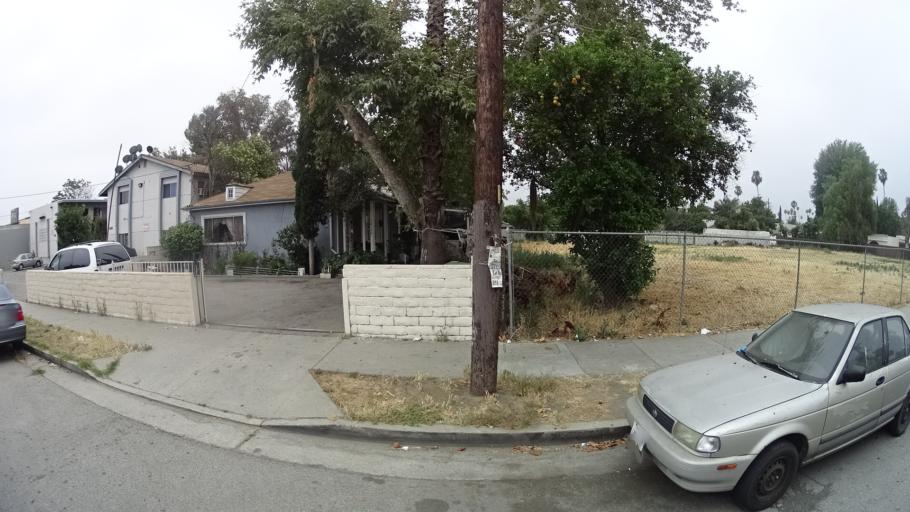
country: US
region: California
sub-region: Los Angeles County
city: Van Nuys
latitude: 34.1939
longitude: -118.4415
